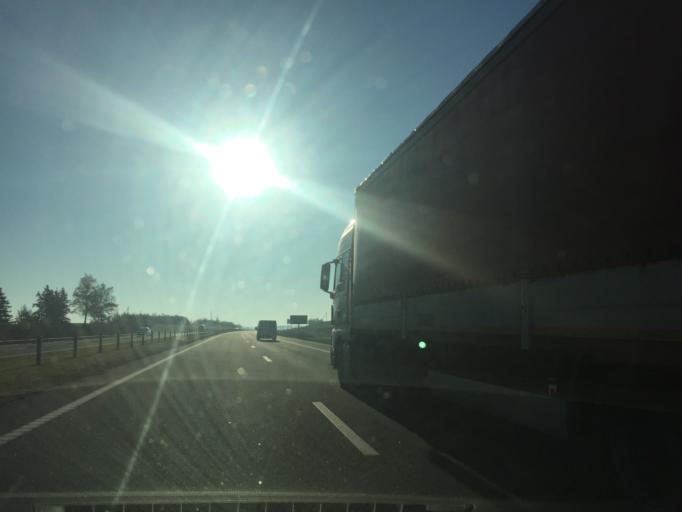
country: BY
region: Minsk
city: Luhavaya Slabada
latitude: 53.7771
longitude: 27.8507
